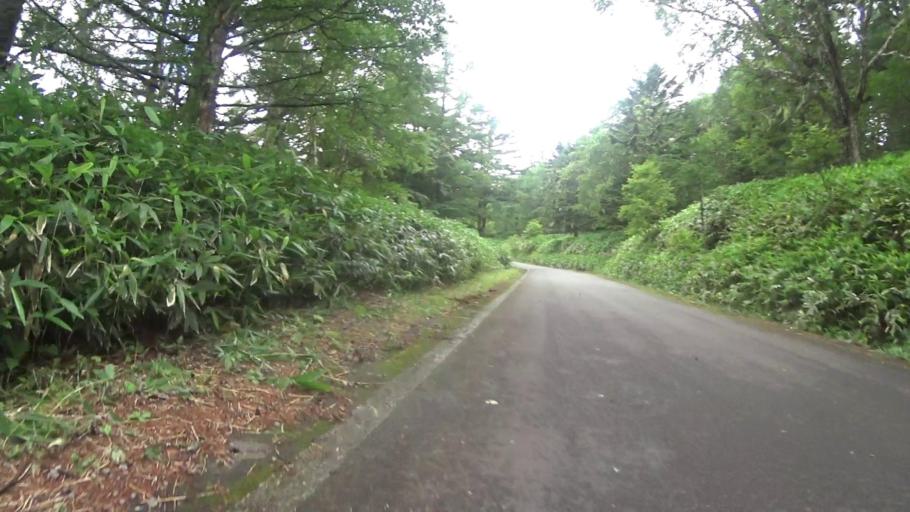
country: JP
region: Nagano
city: Saku
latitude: 36.1150
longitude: 138.3308
